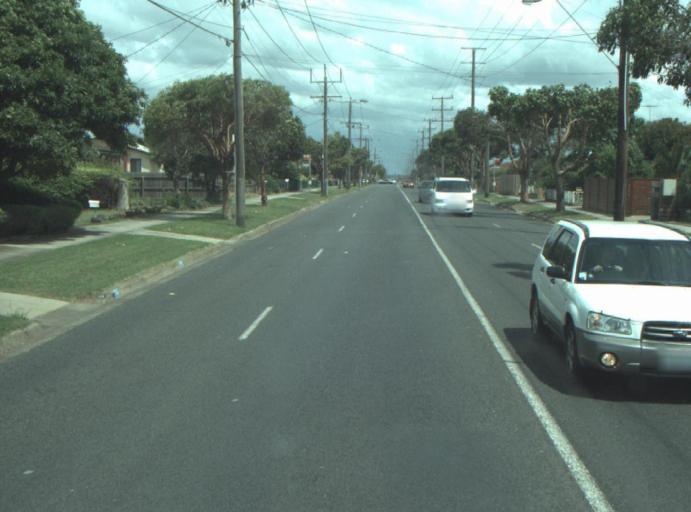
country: AU
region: Victoria
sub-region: Greater Geelong
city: Bell Park
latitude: -38.0879
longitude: 144.3479
